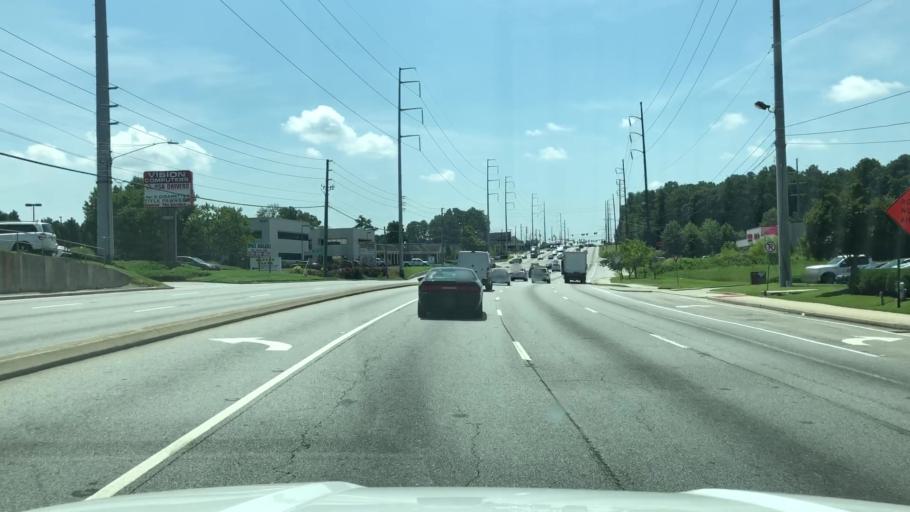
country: US
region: Georgia
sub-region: Gwinnett County
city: Norcross
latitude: 33.9202
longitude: -84.2107
